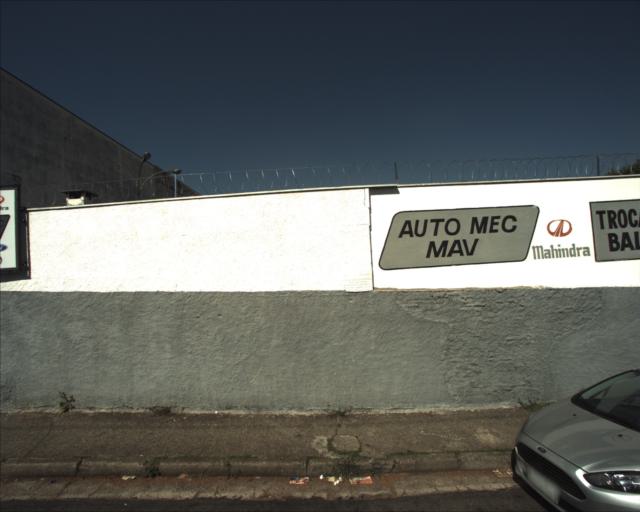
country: BR
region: Sao Paulo
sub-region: Sorocaba
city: Sorocaba
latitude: -23.4969
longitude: -47.4420
